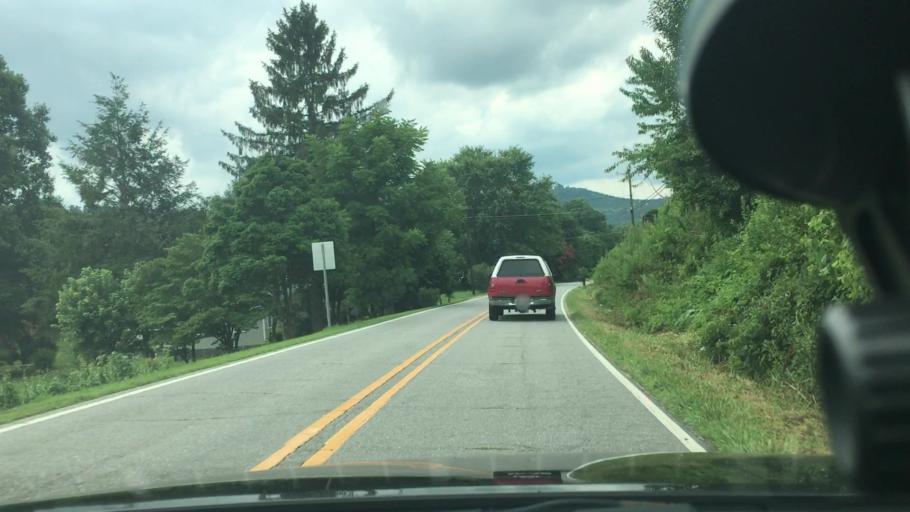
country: US
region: North Carolina
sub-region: McDowell County
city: West Marion
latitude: 35.6499
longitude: -82.0148
